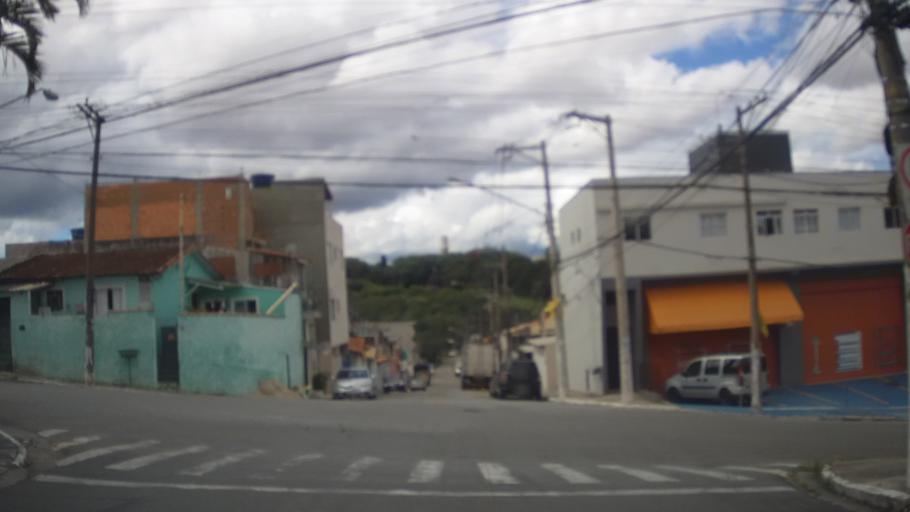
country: BR
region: Sao Paulo
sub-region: Guarulhos
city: Guarulhos
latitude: -23.4784
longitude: -46.5507
